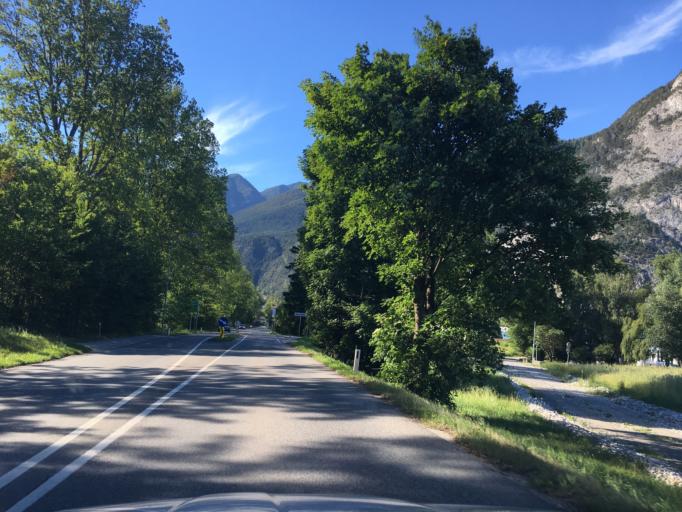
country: AT
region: Tyrol
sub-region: Politischer Bezirk Innsbruck Land
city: Kematen in Tirol
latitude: 47.2598
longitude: 11.2655
